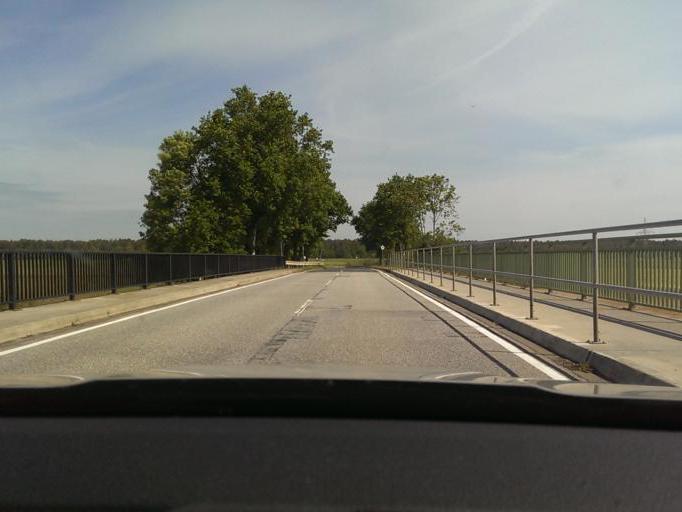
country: DE
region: Lower Saxony
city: Wietze
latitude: 52.6707
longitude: 9.7744
